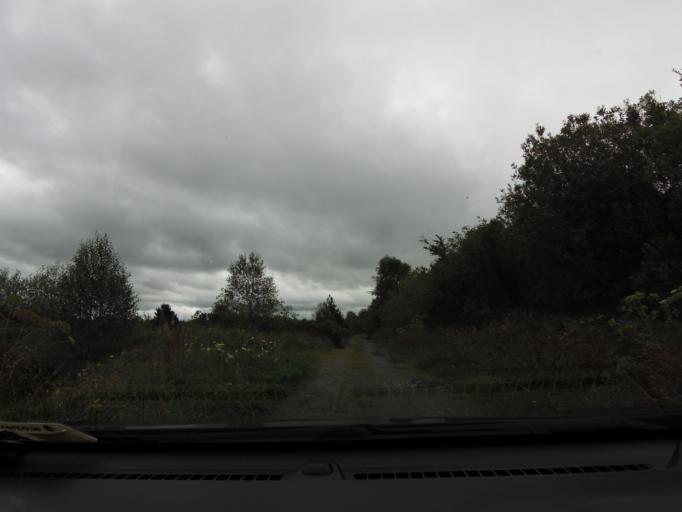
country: IE
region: Connaught
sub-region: County Galway
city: Athenry
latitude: 53.3026
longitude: -8.6538
